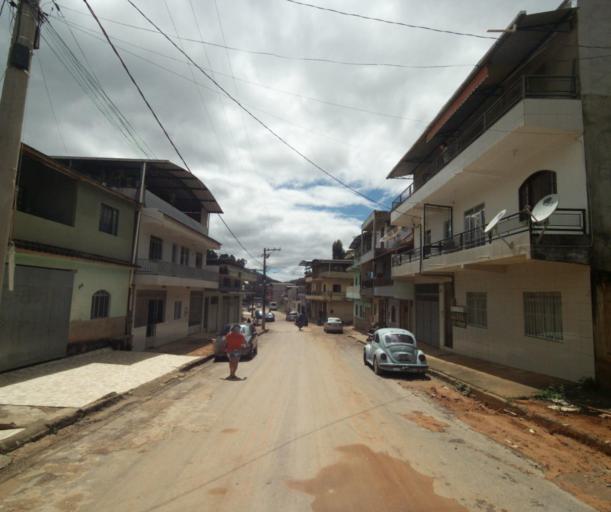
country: BR
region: Espirito Santo
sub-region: Irupi
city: Irupi
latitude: -20.3500
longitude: -41.6467
